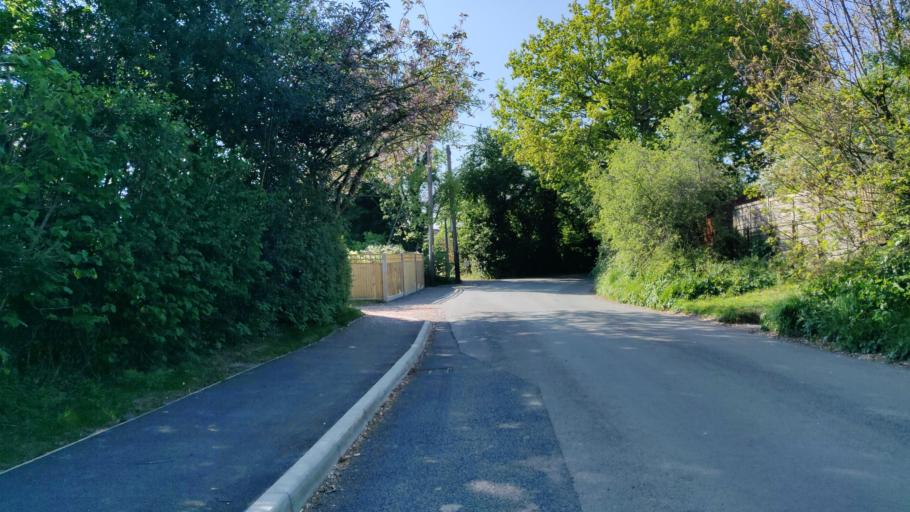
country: GB
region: England
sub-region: West Sussex
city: Southwater
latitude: 51.0286
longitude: -0.3963
